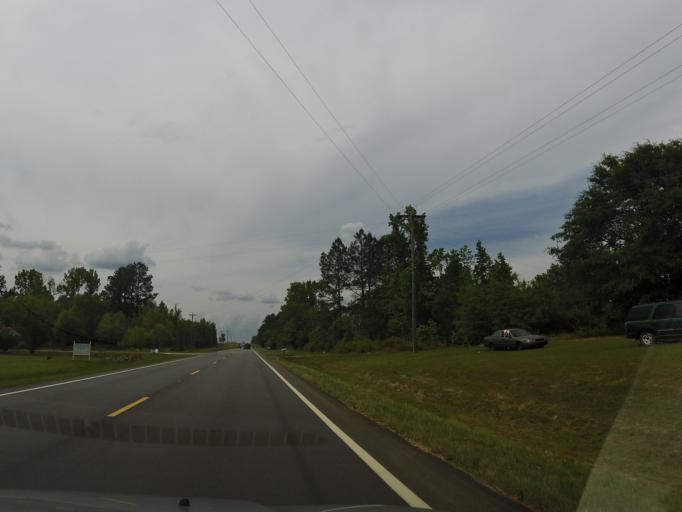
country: US
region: Georgia
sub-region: McDuffie County
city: Thomson
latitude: 33.3554
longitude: -82.4628
